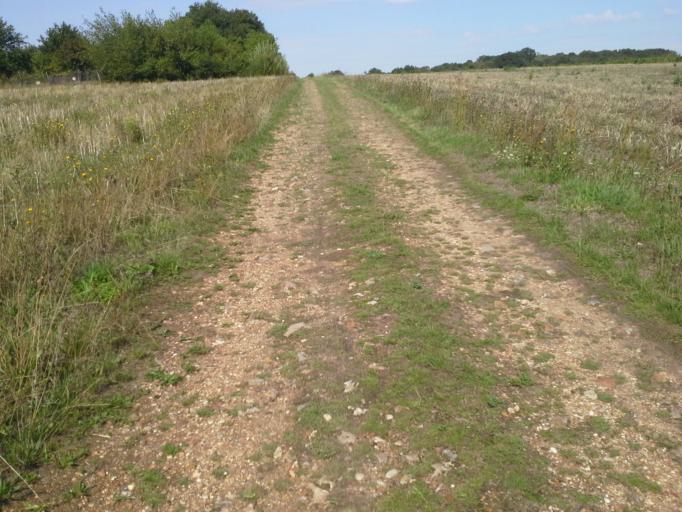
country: FR
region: Centre
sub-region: Departement du Loir-et-Cher
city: Villiers-sur-Loir
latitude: 47.8126
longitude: 0.9907
